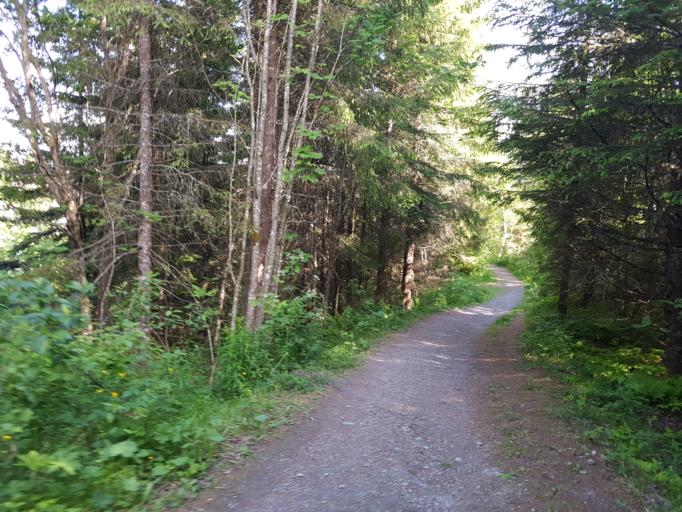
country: NO
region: Sor-Trondelag
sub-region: Trondheim
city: Trondheim
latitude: 63.3992
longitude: 10.3222
